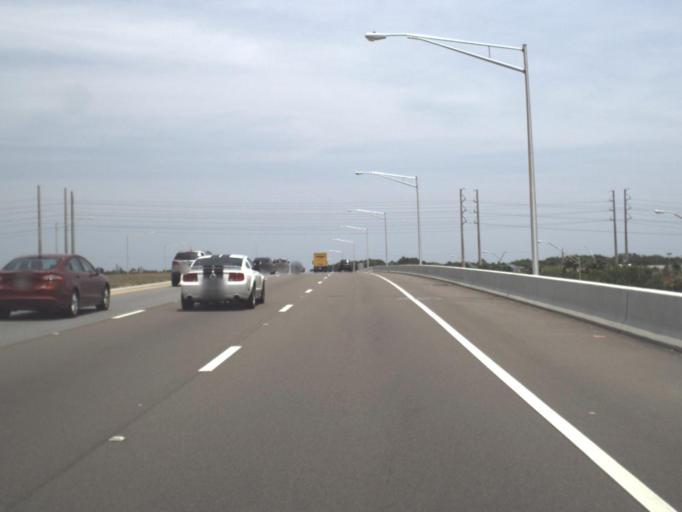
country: US
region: Florida
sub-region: Duval County
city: Atlantic Beach
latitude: 30.3199
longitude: -81.4916
